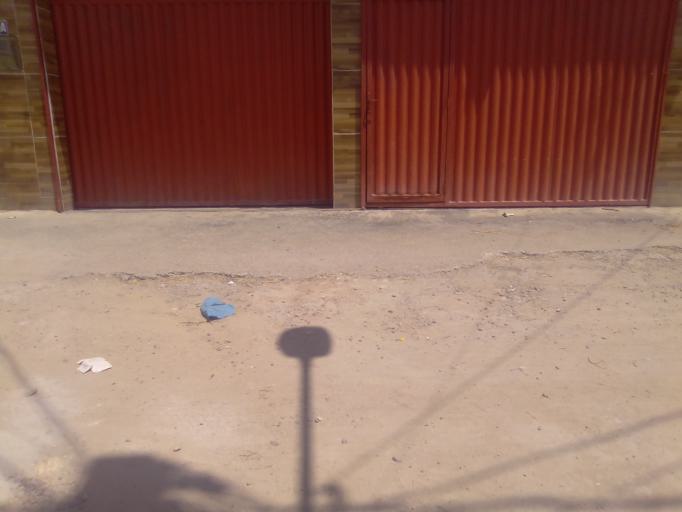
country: BR
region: Pernambuco
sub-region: Jaboatao Dos Guararapes
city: Jaboatao dos Guararapes
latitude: -8.0667
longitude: -34.9999
